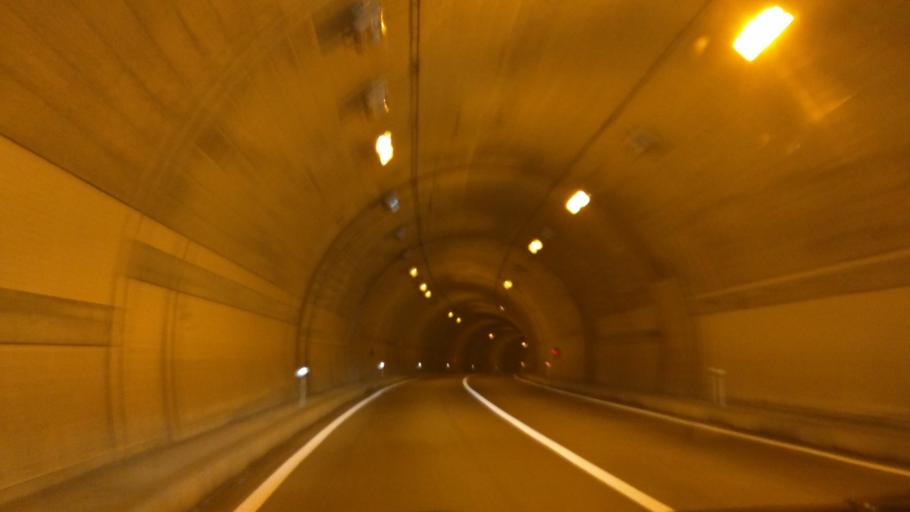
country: JP
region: Fukushima
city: Kitakata
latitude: 37.3623
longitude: 139.8781
